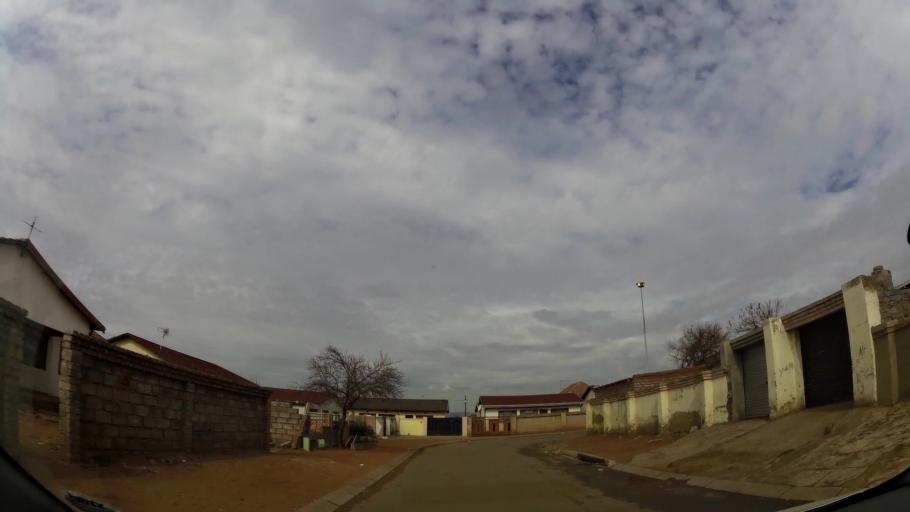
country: ZA
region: Gauteng
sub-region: Ekurhuleni Metropolitan Municipality
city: Germiston
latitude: -26.3756
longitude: 28.1681
